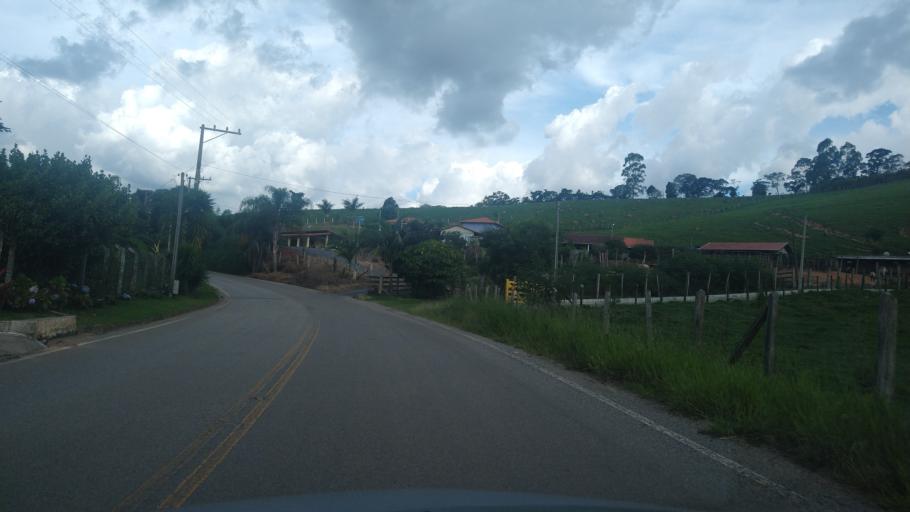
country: BR
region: Minas Gerais
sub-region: Extrema
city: Extrema
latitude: -22.7611
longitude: -46.3339
